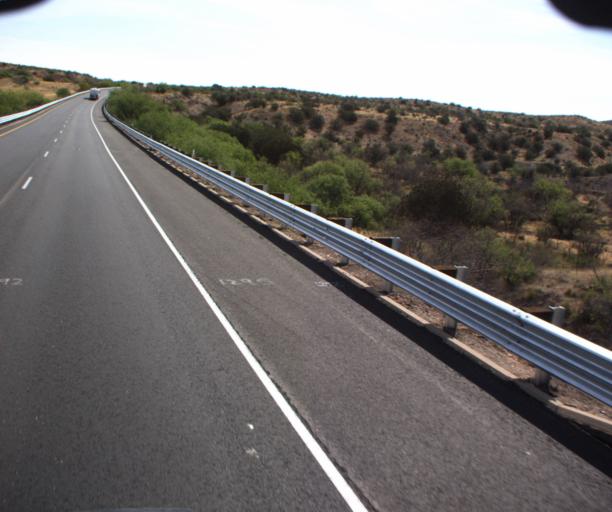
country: US
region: Arizona
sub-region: Pima County
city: Vail
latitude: 31.9977
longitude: -110.6335
